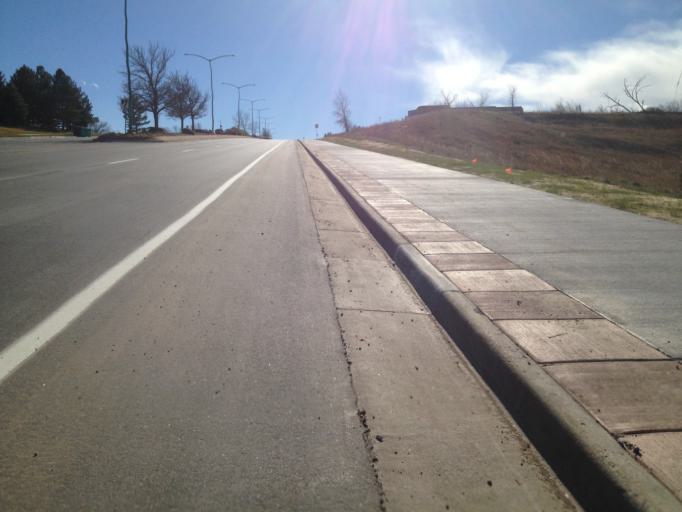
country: US
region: Colorado
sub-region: Boulder County
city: Superior
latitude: 39.9493
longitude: -105.1648
